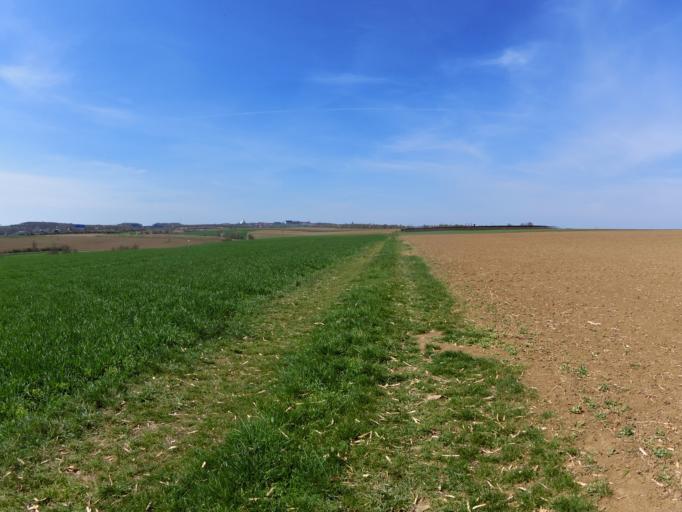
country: DE
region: Bavaria
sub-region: Regierungsbezirk Unterfranken
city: Mainstockheim
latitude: 49.7884
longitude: 10.1213
